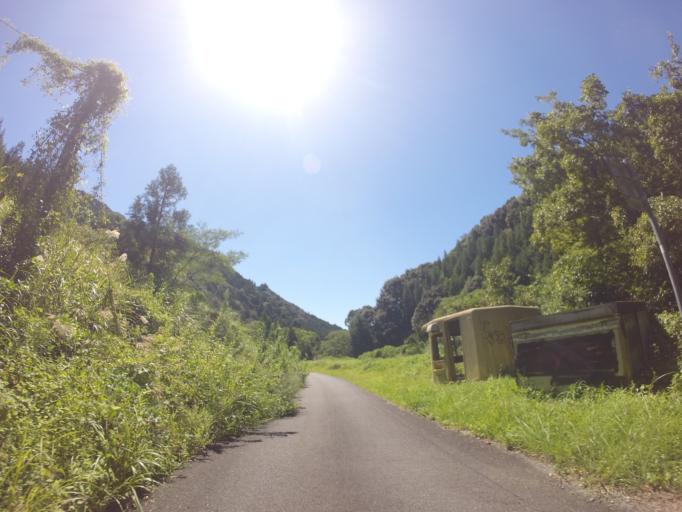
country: JP
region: Shizuoka
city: Kanaya
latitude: 34.8959
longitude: 138.1517
